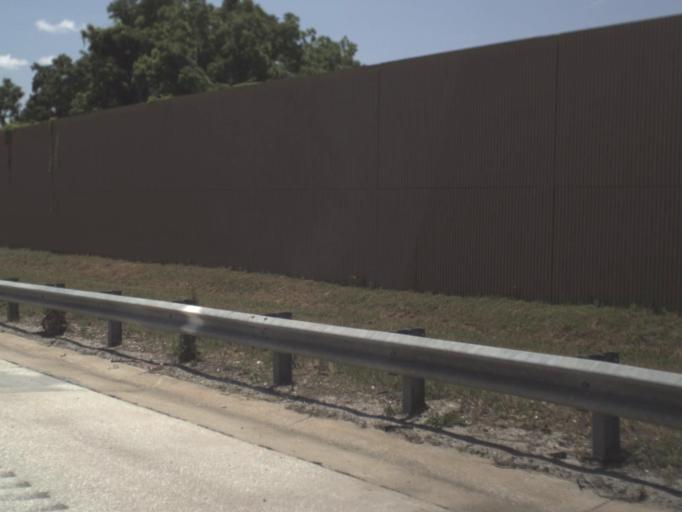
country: US
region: Florida
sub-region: Duval County
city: Jacksonville
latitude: 30.2985
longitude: -81.6383
